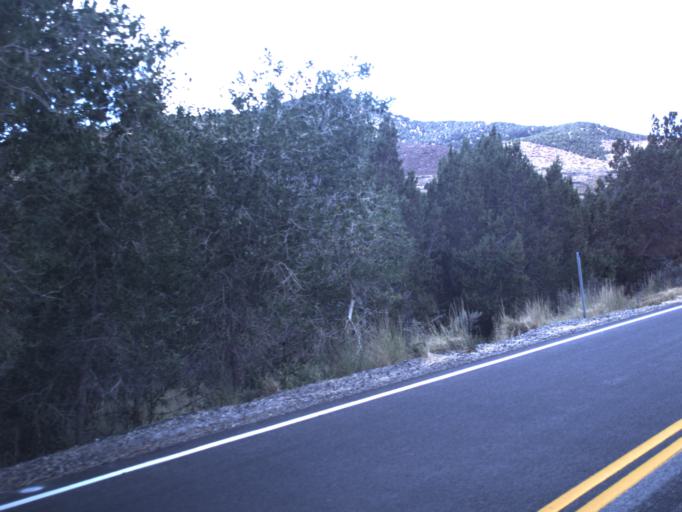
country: US
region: Utah
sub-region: Tooele County
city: Grantsville
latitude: 40.3362
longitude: -112.5298
